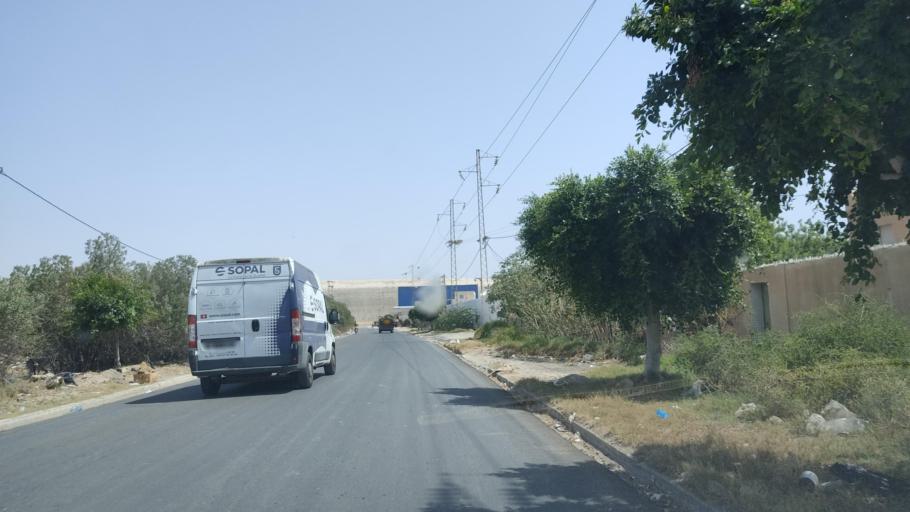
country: TN
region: Safaqis
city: Sfax
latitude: 34.6893
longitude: 10.7256
